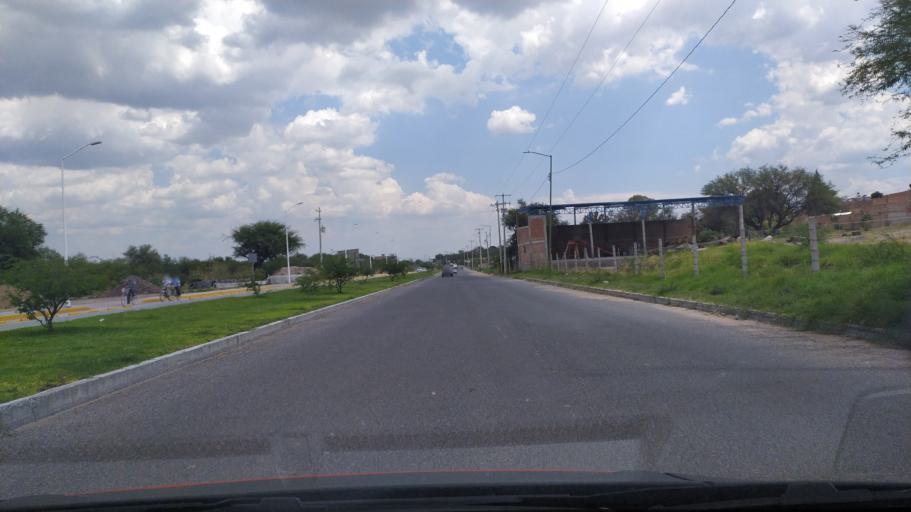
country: MX
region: Guanajuato
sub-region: Purisima del Rincon
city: Potrerillos (Guanajal)
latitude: 21.0488
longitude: -101.8692
